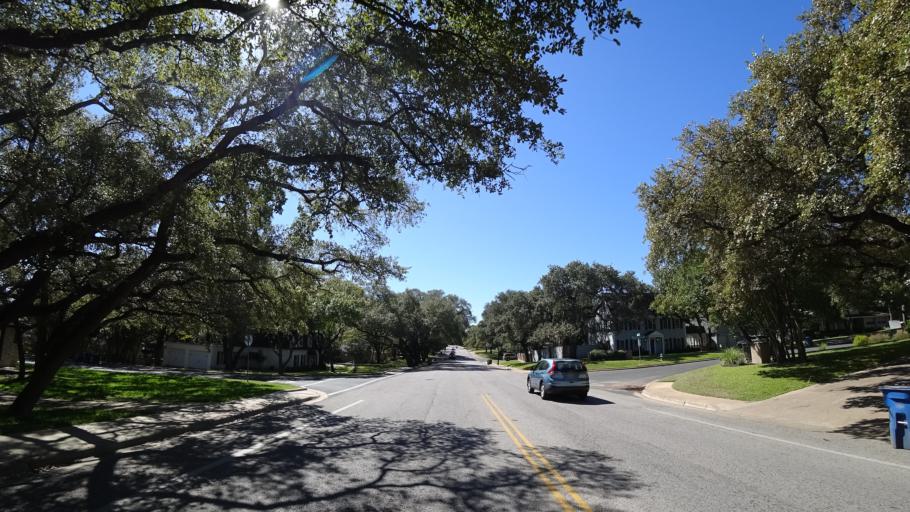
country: US
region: Texas
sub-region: Travis County
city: West Lake Hills
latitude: 30.3627
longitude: -97.7648
